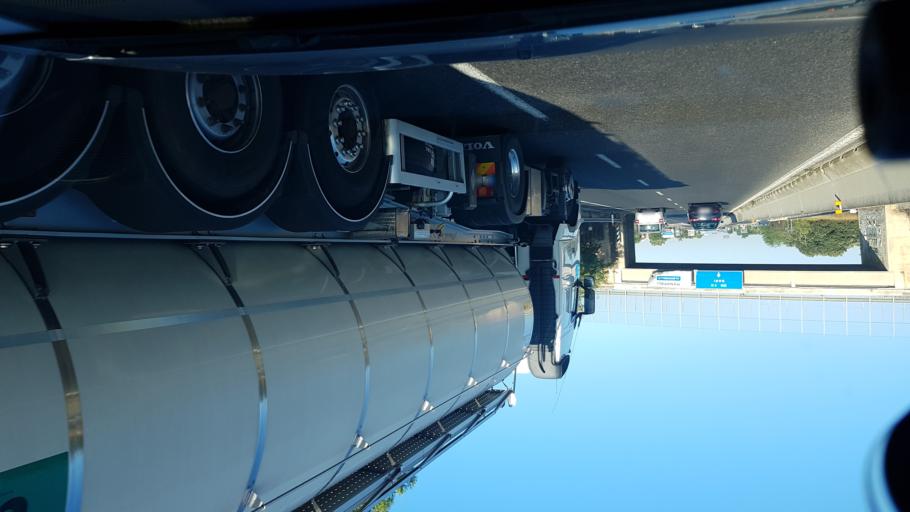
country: IT
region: Apulia
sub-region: Provincia di Bari
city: Monopoli
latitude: 40.9351
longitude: 17.2934
